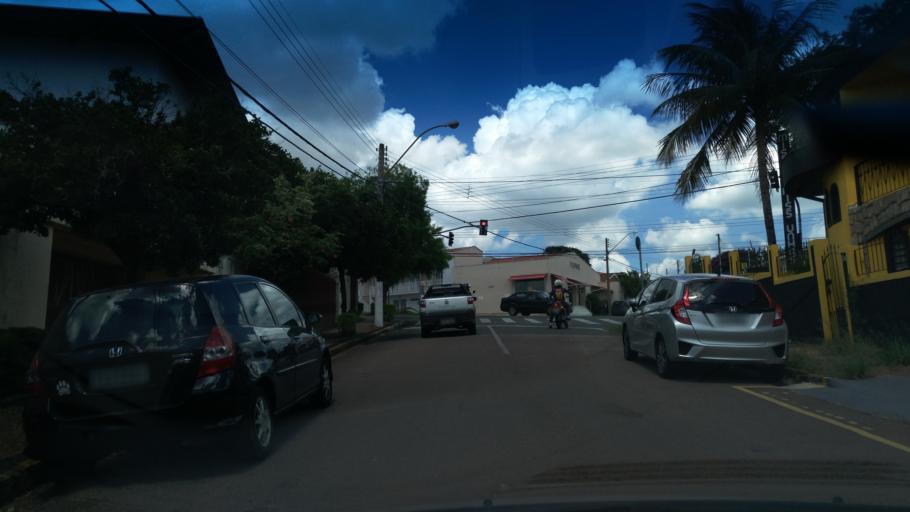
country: BR
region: Sao Paulo
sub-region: Valinhos
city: Valinhos
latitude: -22.9675
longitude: -47.0043
